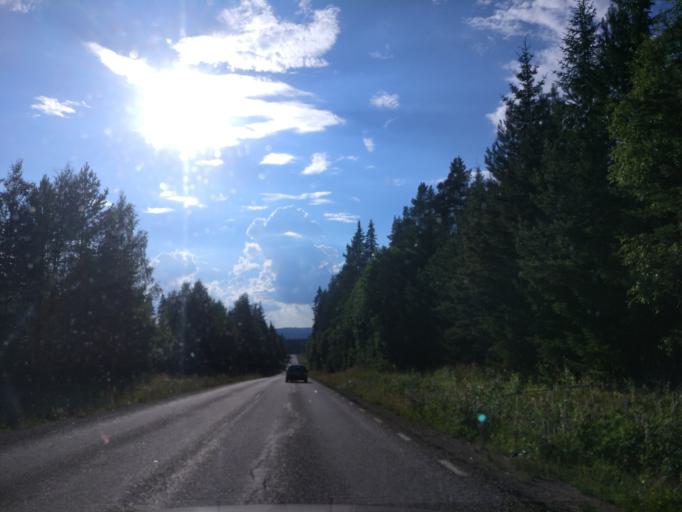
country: SE
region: Dalarna
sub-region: Ludvika Kommun
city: Ludvika
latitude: 60.2649
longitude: 15.0468
